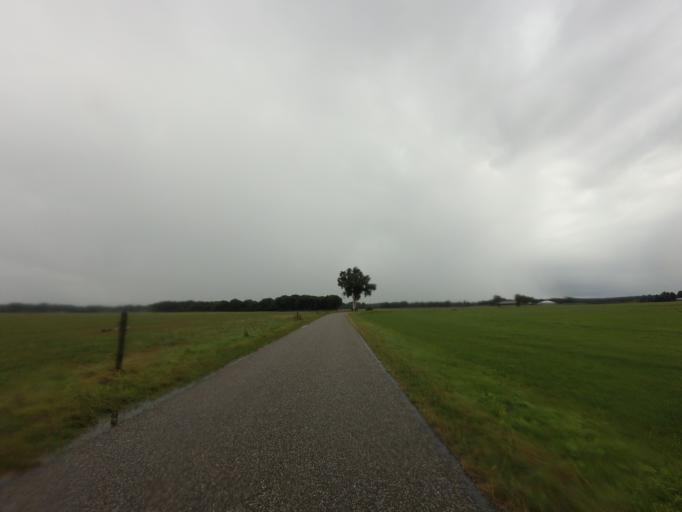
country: NL
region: Drenthe
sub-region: Gemeente Hoogeveen
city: Hoogeveen
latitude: 52.6295
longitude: 6.4039
